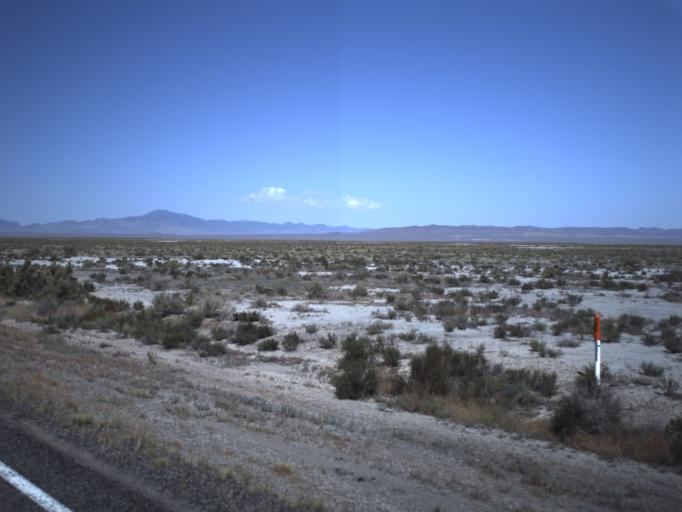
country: US
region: Utah
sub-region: Millard County
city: Delta
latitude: 39.3057
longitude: -112.7986
